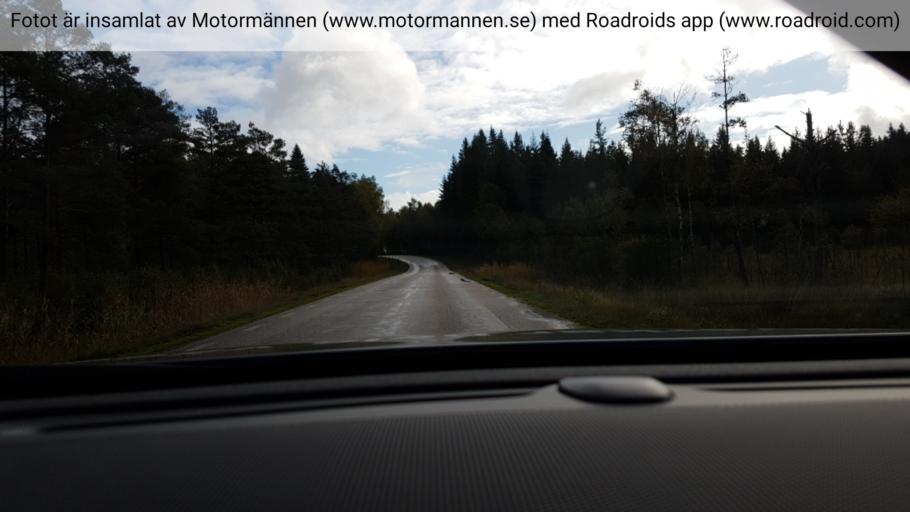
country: SE
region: Vaestra Goetaland
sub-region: Marks Kommun
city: Fritsla
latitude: 57.4020
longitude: 12.8744
